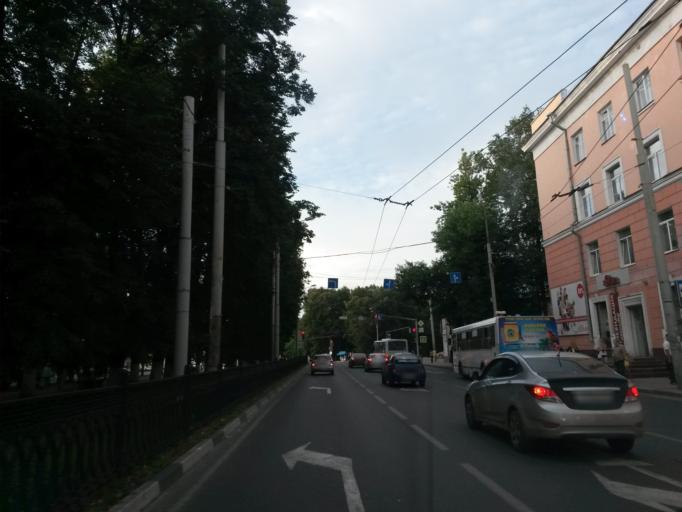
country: RU
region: Jaroslavl
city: Yaroslavl
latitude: 57.6306
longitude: 39.8879
